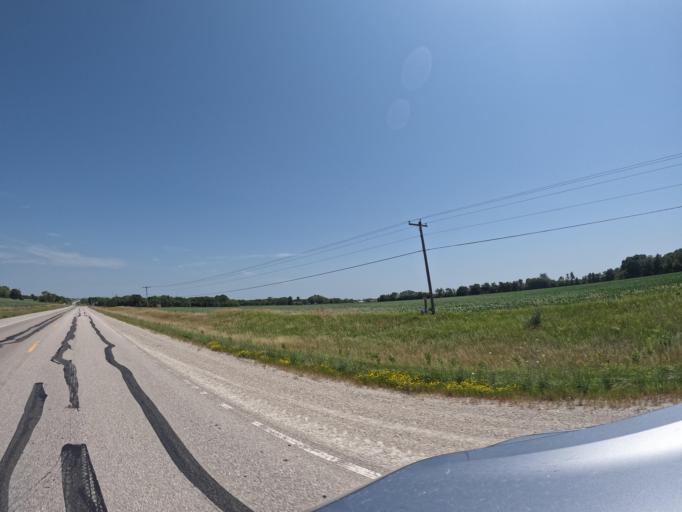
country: US
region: Iowa
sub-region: Henry County
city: Mount Pleasant
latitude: 40.9671
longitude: -91.6169
